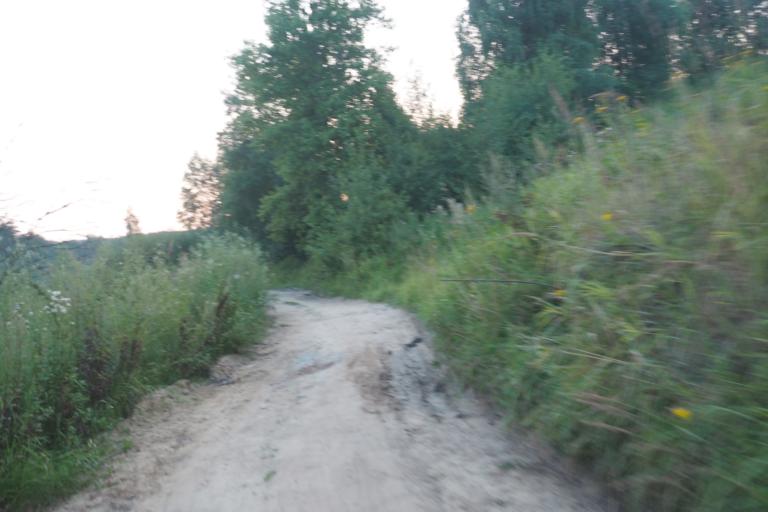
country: RU
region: Moscow
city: Orekhovo-Borisovo Severnoye
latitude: 55.6026
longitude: 37.7002
